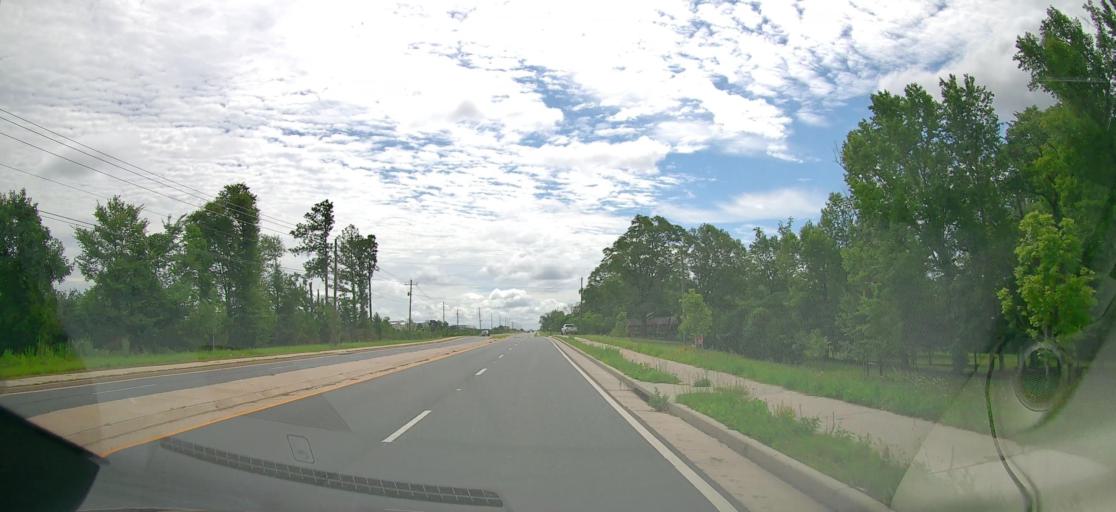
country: US
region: Georgia
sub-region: Houston County
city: Centerville
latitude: 32.6835
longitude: -83.6544
